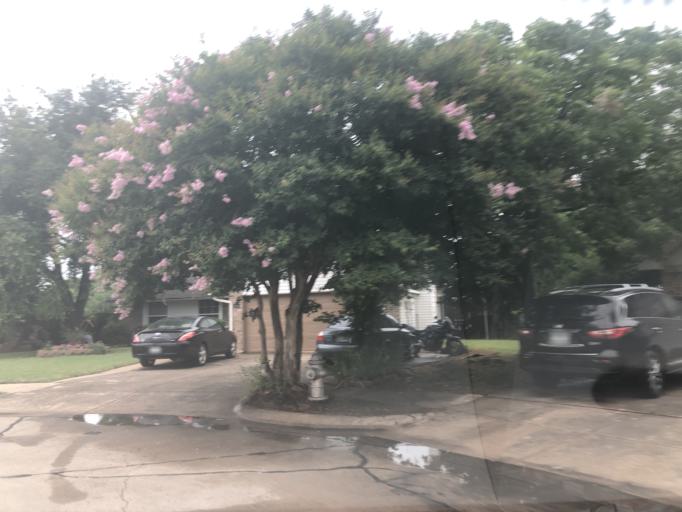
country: US
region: Texas
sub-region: Dallas County
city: Irving
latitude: 32.7897
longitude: -96.9639
